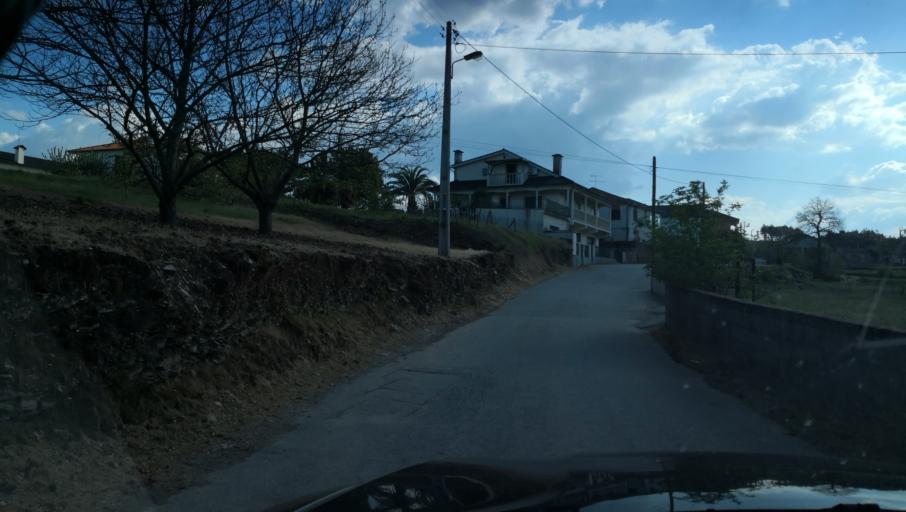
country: PT
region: Vila Real
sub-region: Sabrosa
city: Vilela
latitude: 41.2425
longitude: -7.6525
